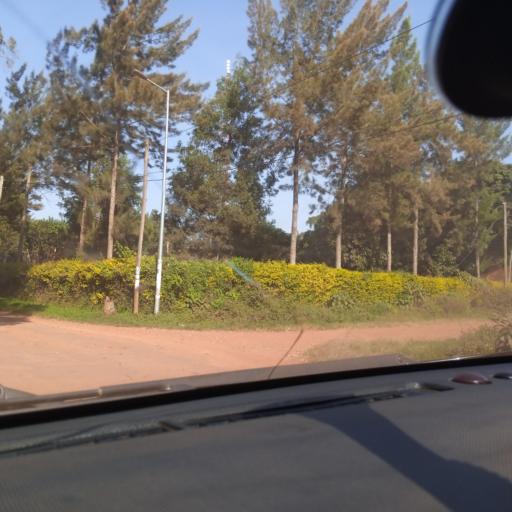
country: UG
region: Central Region
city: Masaka
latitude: -0.3362
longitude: 31.7359
